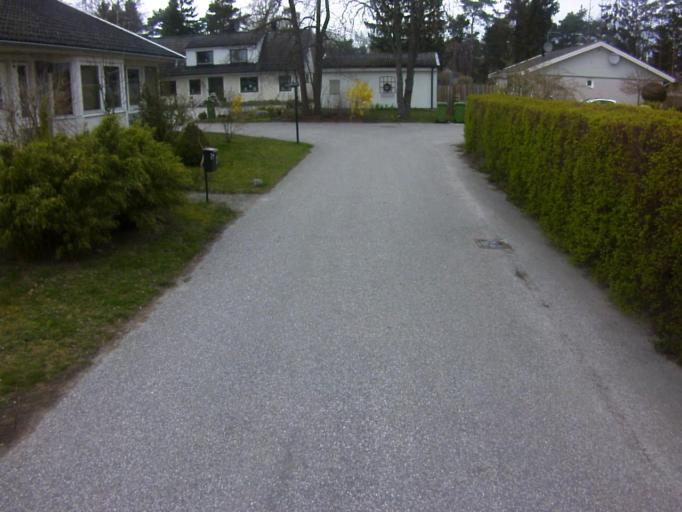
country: SE
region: Skane
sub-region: Kavlinge Kommun
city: Hofterup
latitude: 55.7971
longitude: 12.9841
